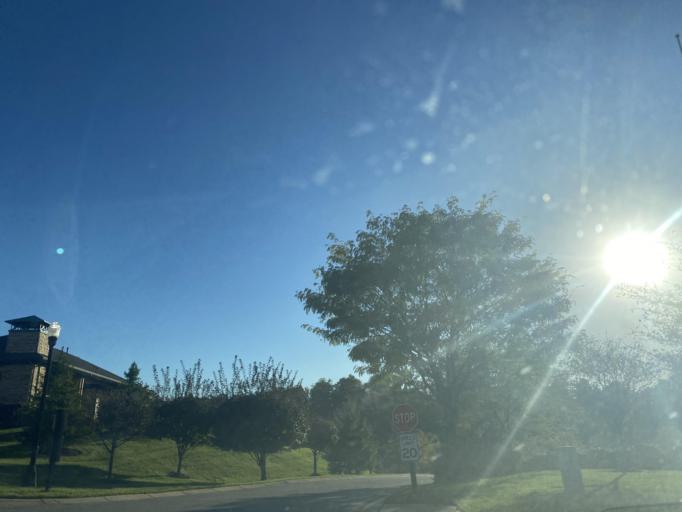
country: US
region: Kentucky
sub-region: Campbell County
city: Dayton
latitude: 39.1102
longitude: -84.4647
